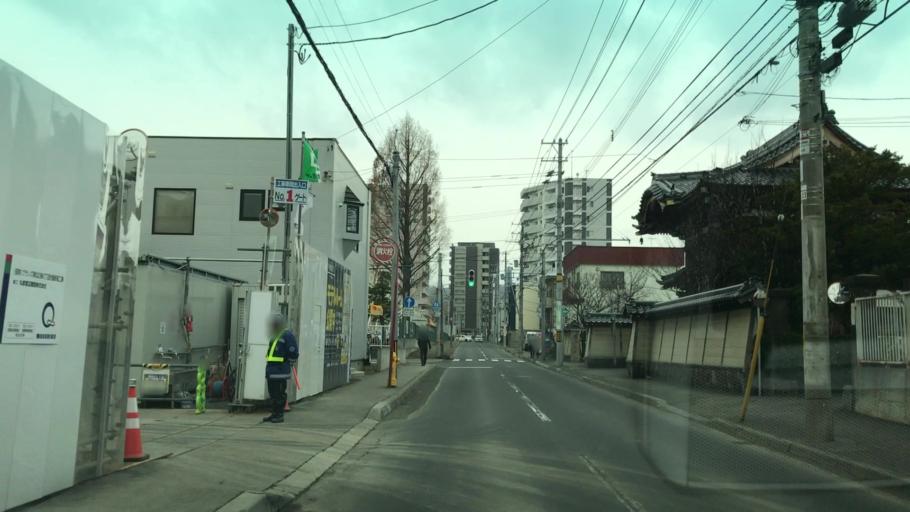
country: JP
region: Hokkaido
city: Sapporo
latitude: 43.0760
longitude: 141.2998
